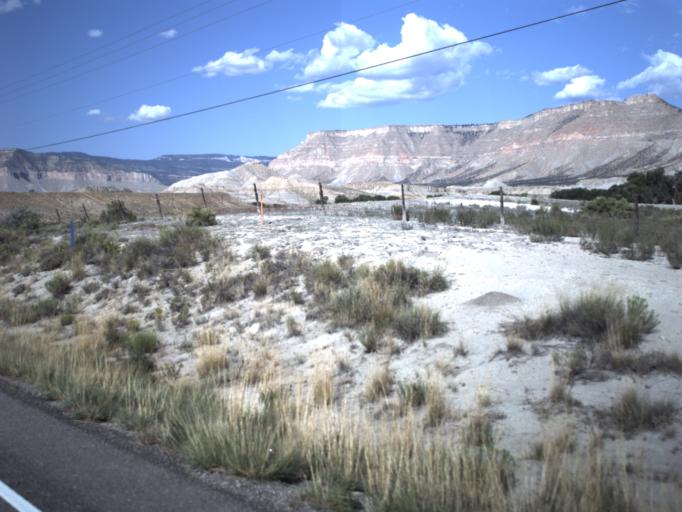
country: US
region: Utah
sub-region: Emery County
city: Ferron
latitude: 39.1234
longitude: -111.1112
